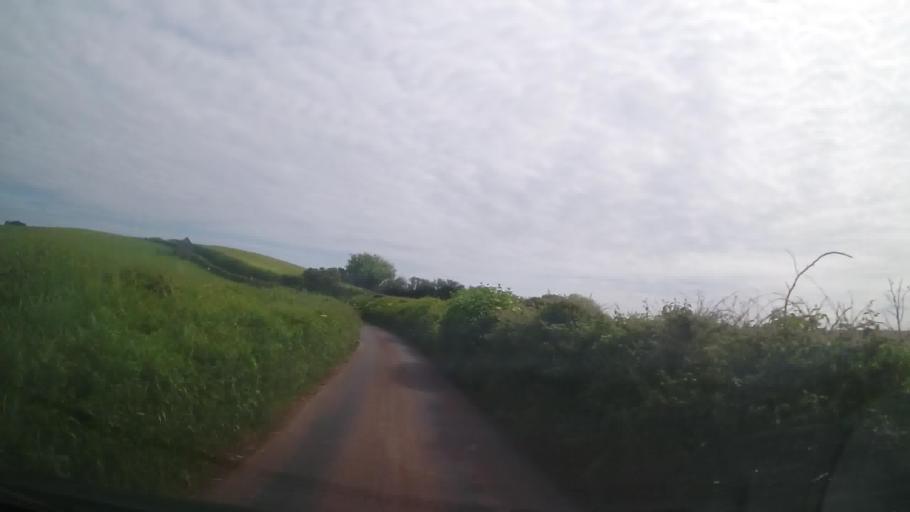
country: GB
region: England
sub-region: Devon
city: Salcombe
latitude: 50.2400
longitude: -3.6785
